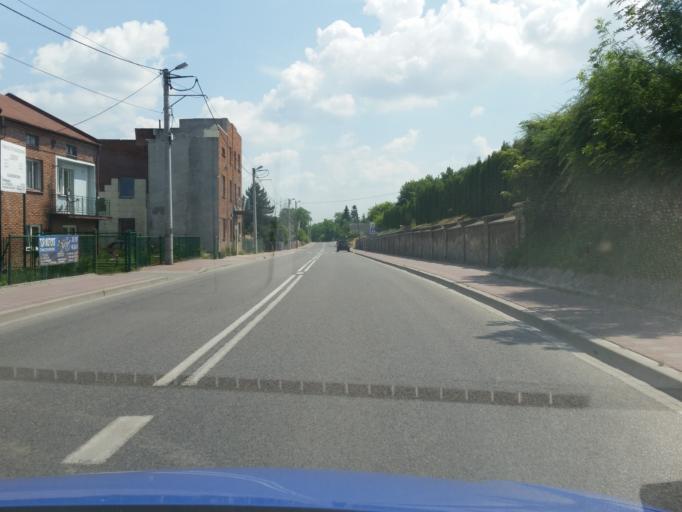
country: PL
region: Swietokrzyskie
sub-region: Powiat kazimierski
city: Skalbmierz
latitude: 50.3168
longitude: 20.4025
